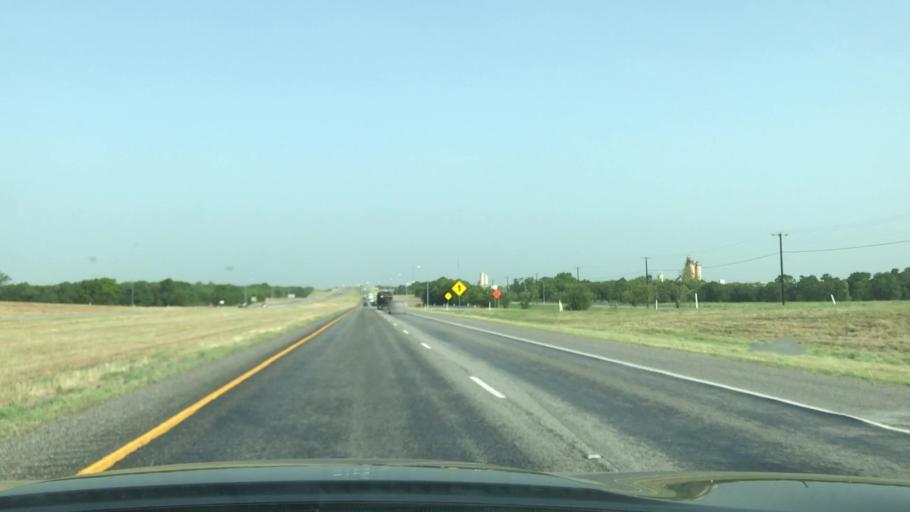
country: US
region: Texas
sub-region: Kaufman County
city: Talty
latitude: 32.7308
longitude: -96.3416
